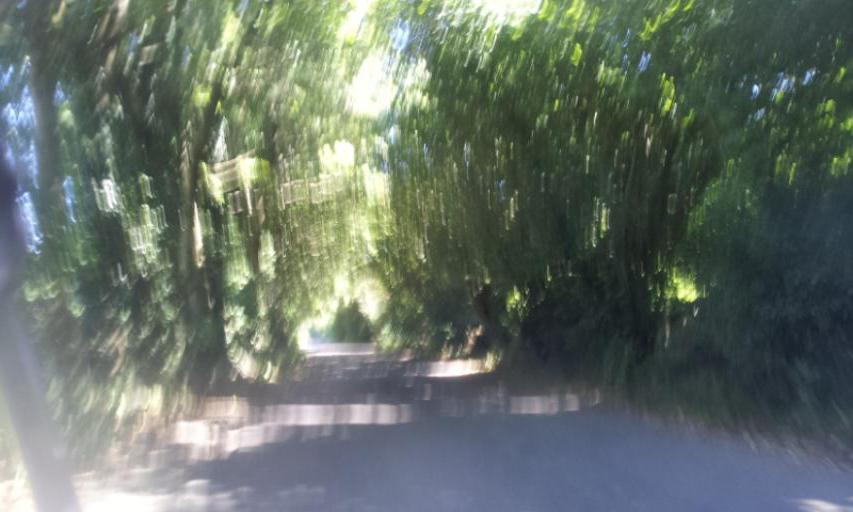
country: GB
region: England
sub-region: Kent
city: Sittingbourne
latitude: 51.3045
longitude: 0.7166
